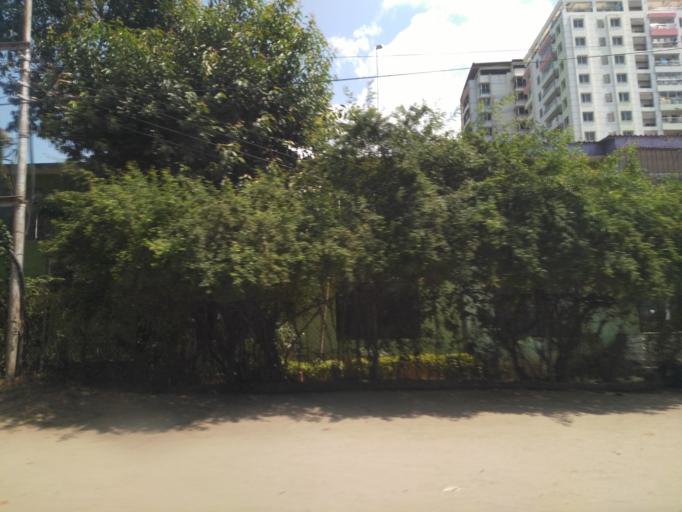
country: TZ
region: Dar es Salaam
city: Dar es Salaam
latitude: -6.8047
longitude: 39.2828
